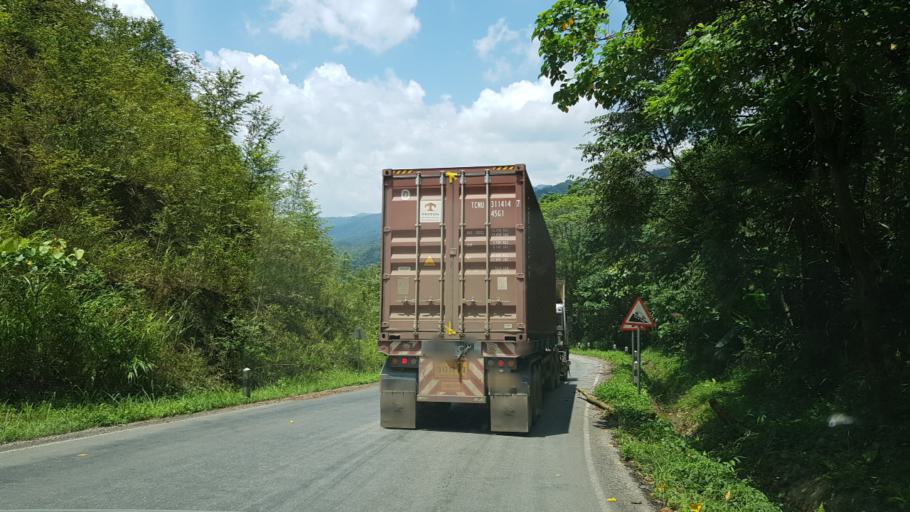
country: LA
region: Vientiane
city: Muang Kasi
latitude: 19.3685
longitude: 102.1610
